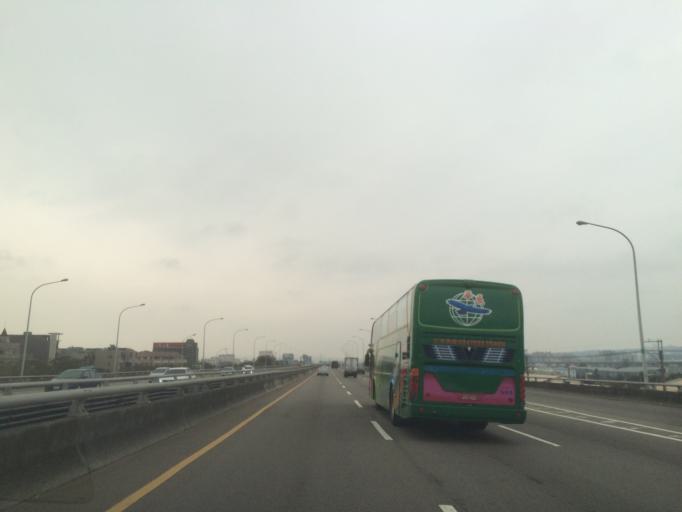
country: TW
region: Taiwan
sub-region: Taichung City
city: Taichung
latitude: 24.1674
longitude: 120.6309
